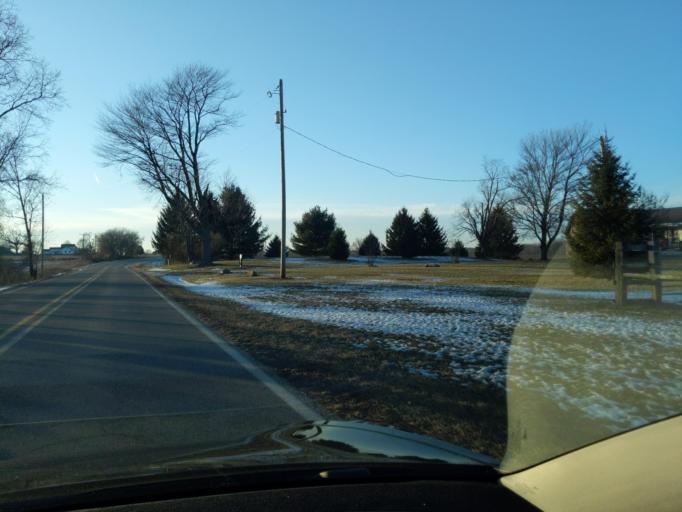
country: US
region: Michigan
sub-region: Ingham County
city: Stockbridge
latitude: 42.4680
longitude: -84.1379
